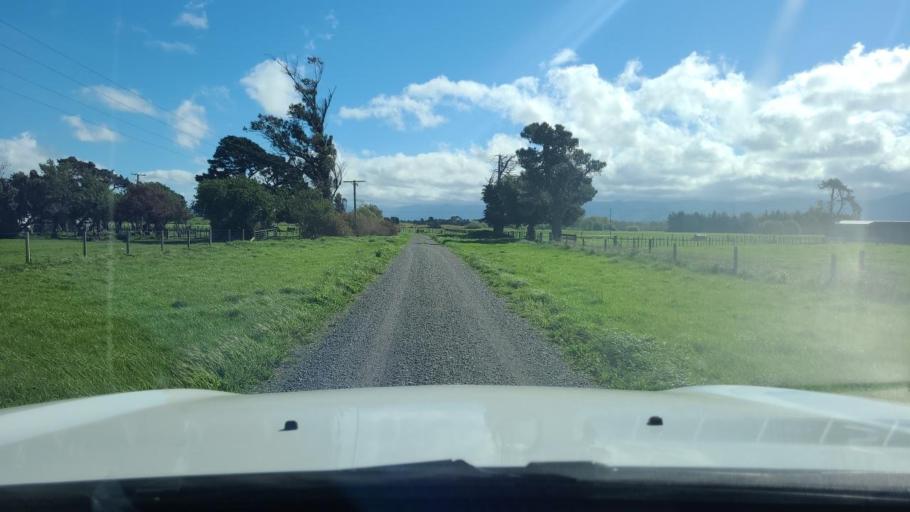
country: NZ
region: Wellington
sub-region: South Wairarapa District
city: Waipawa
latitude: -41.1877
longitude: 175.3588
